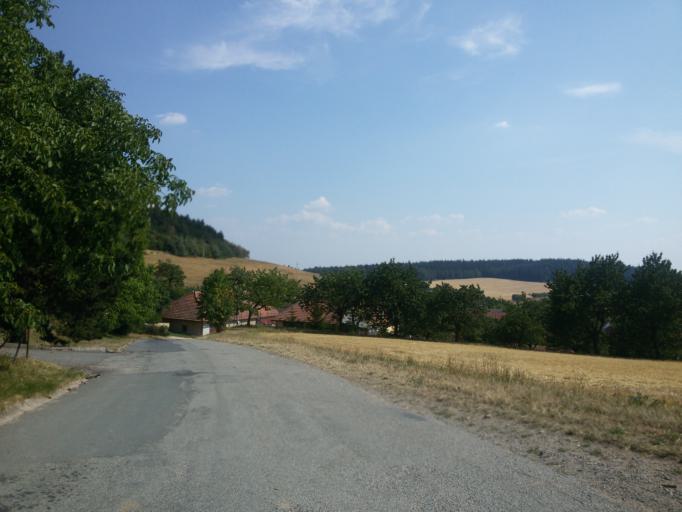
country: CZ
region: South Moravian
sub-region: Okres Brno-Venkov
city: Lomnice
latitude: 49.4458
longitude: 16.4587
